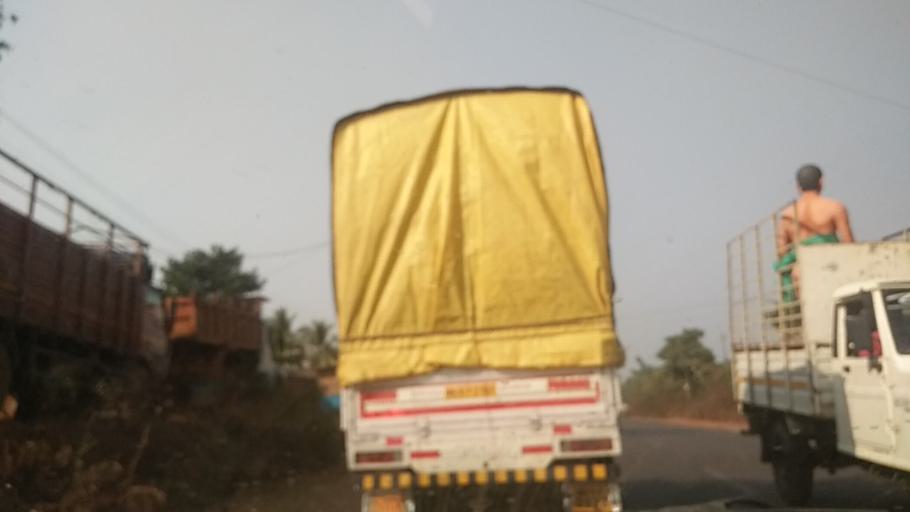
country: IN
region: Goa
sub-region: North Goa
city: Colovale
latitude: 15.6134
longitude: 73.8228
